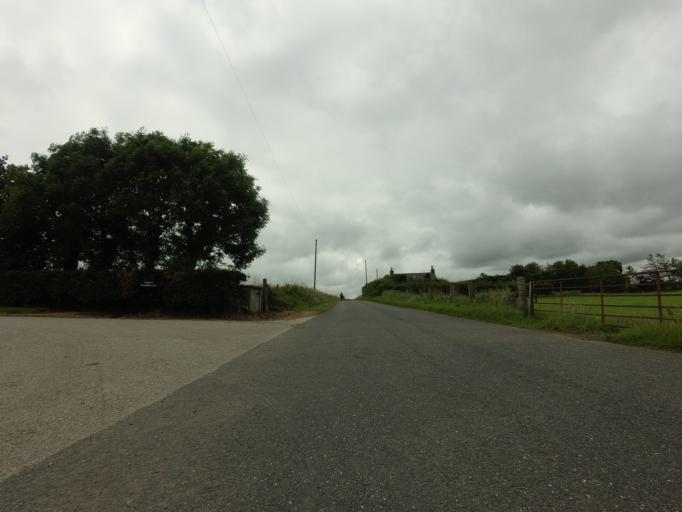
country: GB
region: Scotland
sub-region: Aberdeenshire
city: Turriff
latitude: 57.5352
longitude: -2.4310
